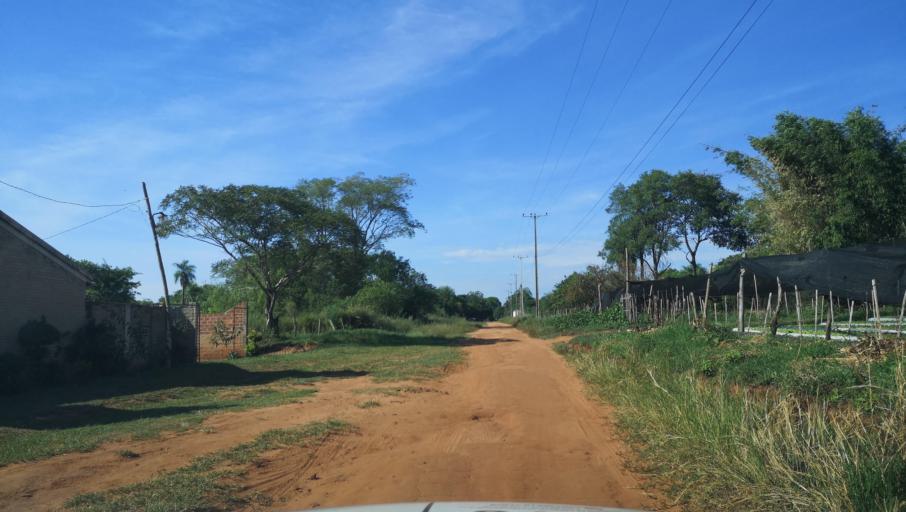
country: PY
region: Misiones
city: Santa Maria
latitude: -26.8731
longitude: -57.0084
